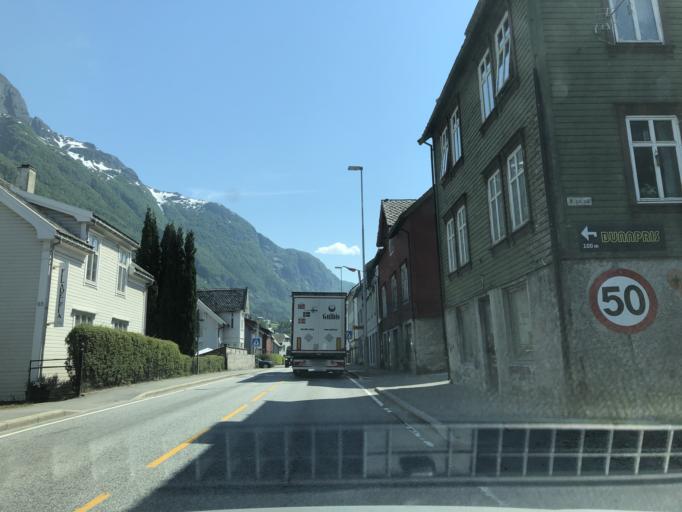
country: NO
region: Hordaland
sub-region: Odda
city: Odda
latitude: 60.0643
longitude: 6.5477
